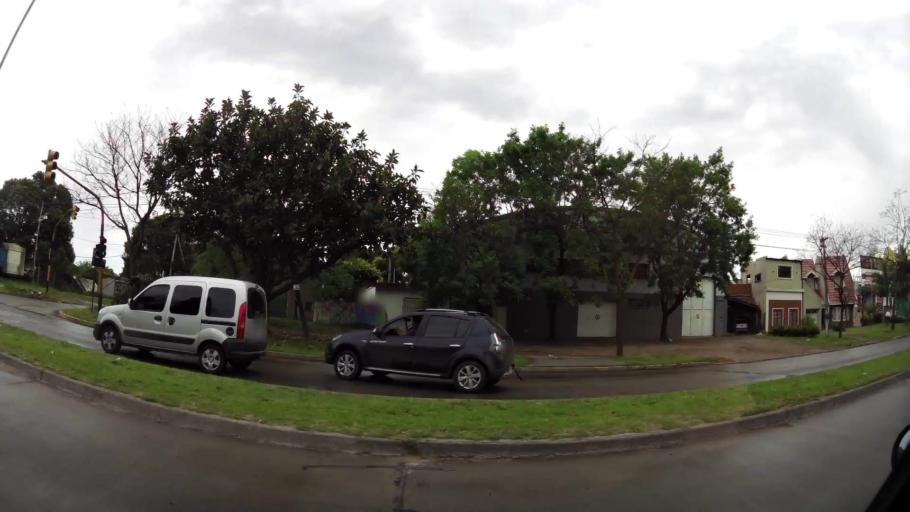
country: AR
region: Buenos Aires
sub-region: Partido de Quilmes
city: Quilmes
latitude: -34.7512
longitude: -58.2182
